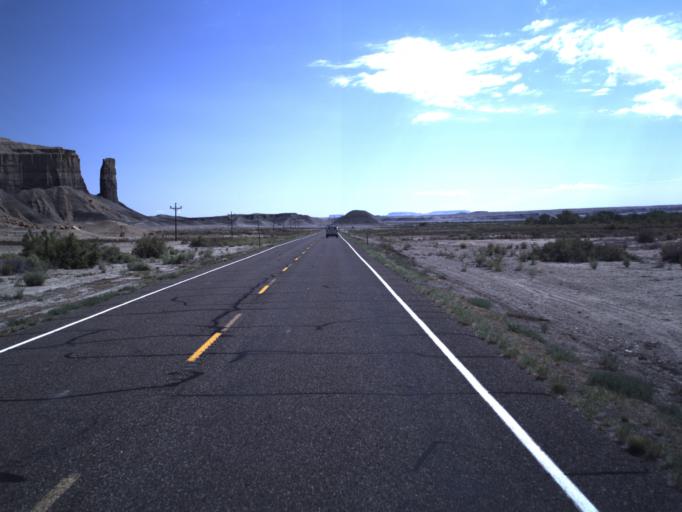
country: US
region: Utah
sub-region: Emery County
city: Ferron
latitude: 38.3650
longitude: -110.8590
